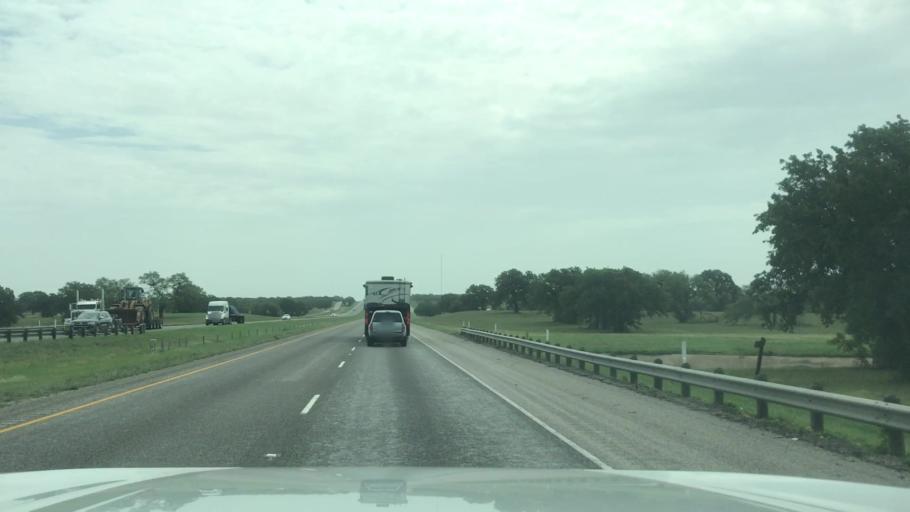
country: US
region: Texas
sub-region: Eastland County
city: Eastland
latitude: 32.3754
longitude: -98.8866
